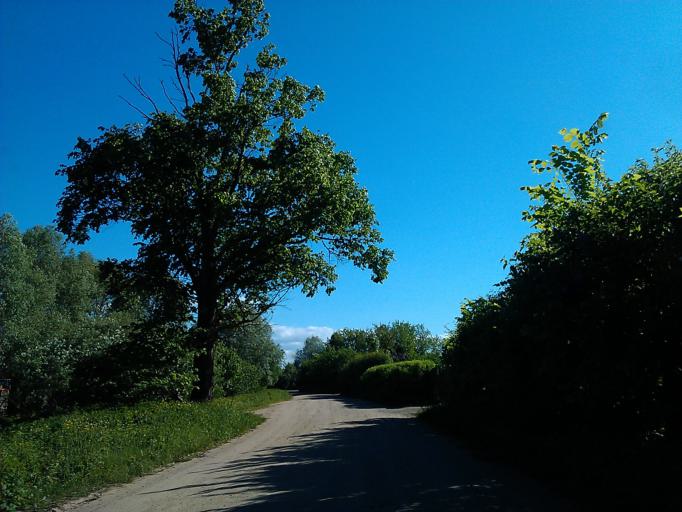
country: LV
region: Adazi
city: Adazi
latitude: 57.0888
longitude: 24.3212
